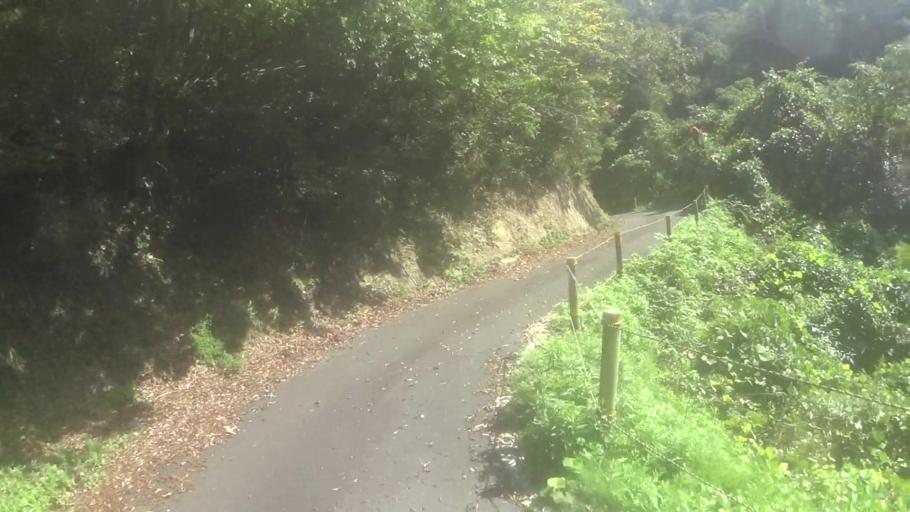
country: JP
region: Kyoto
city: Miyazu
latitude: 35.6690
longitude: 135.1401
